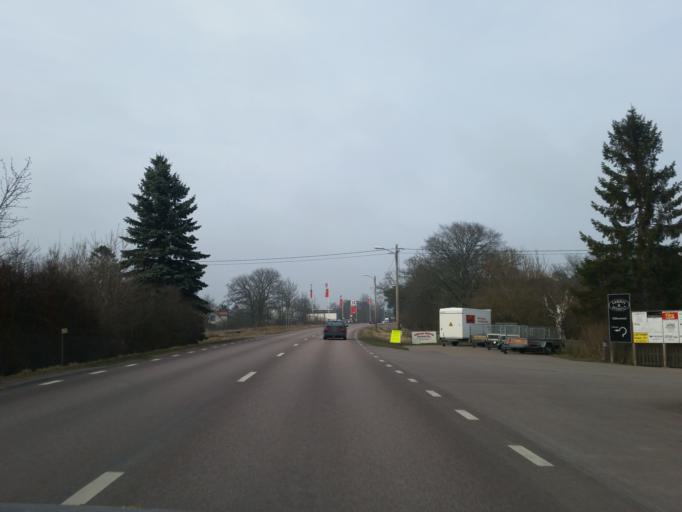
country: SE
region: Kalmar
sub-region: Borgholms Kommun
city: Borgholm
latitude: 57.1613
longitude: 17.0109
